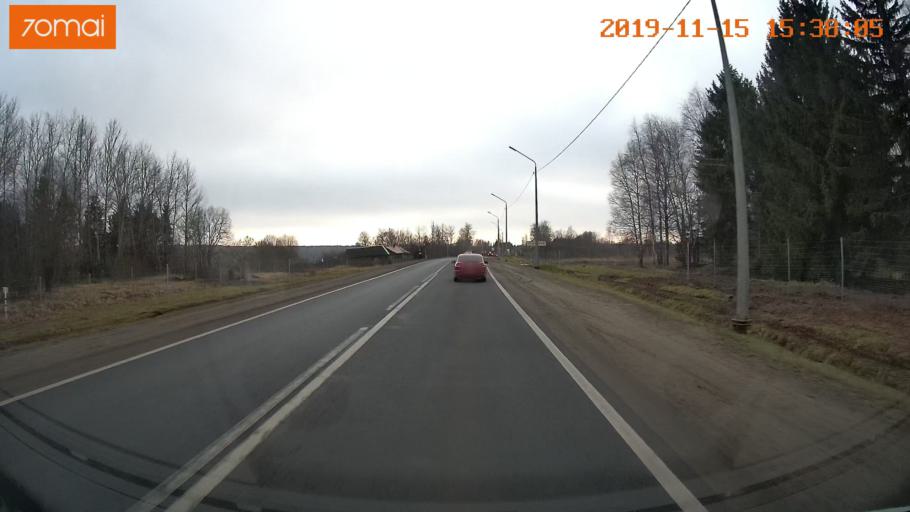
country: RU
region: Jaroslavl
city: Danilov
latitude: 58.0330
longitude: 40.0839
